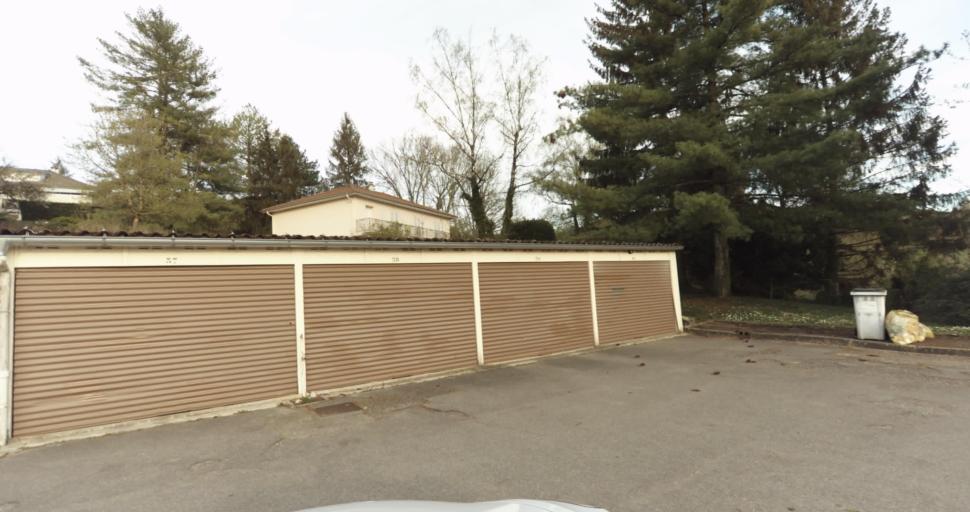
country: FR
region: Rhone-Alpes
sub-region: Departement de l'Ain
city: Amberieu-en-Bugey
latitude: 45.9587
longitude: 5.3662
